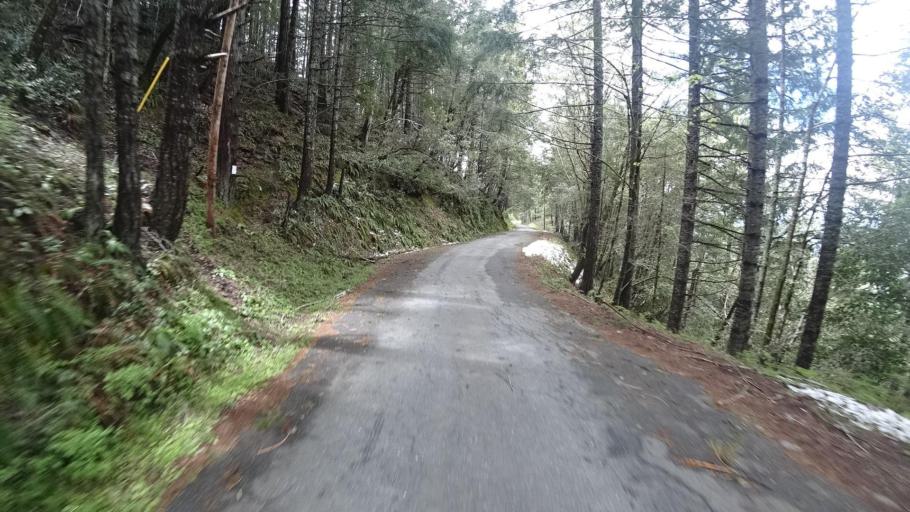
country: US
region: California
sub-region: Humboldt County
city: Blue Lake
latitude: 40.8760
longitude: -123.8813
